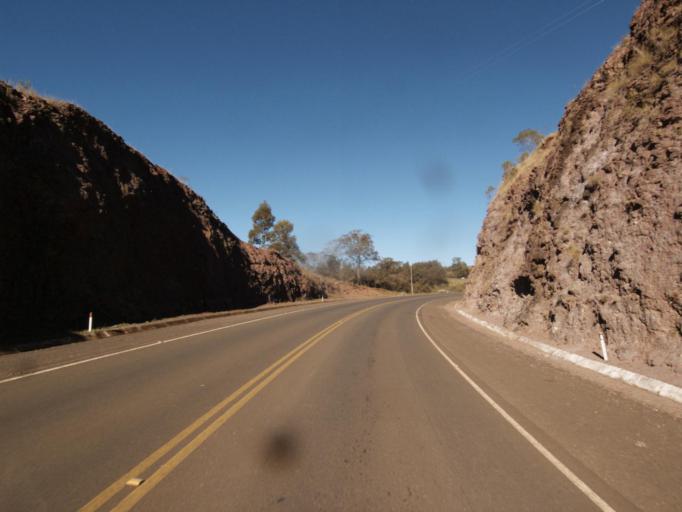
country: AR
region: Misiones
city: Bernardo de Irigoyen
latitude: -26.6974
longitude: -53.5347
